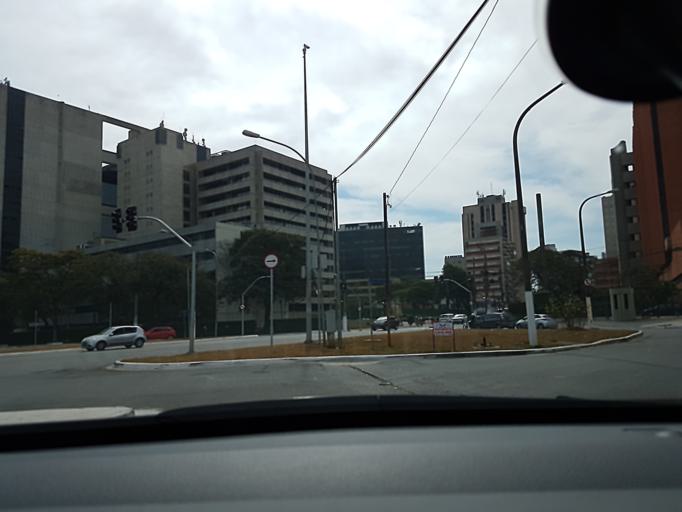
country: BR
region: Sao Paulo
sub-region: Taboao Da Serra
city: Taboao da Serra
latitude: -23.6341
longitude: -46.7117
